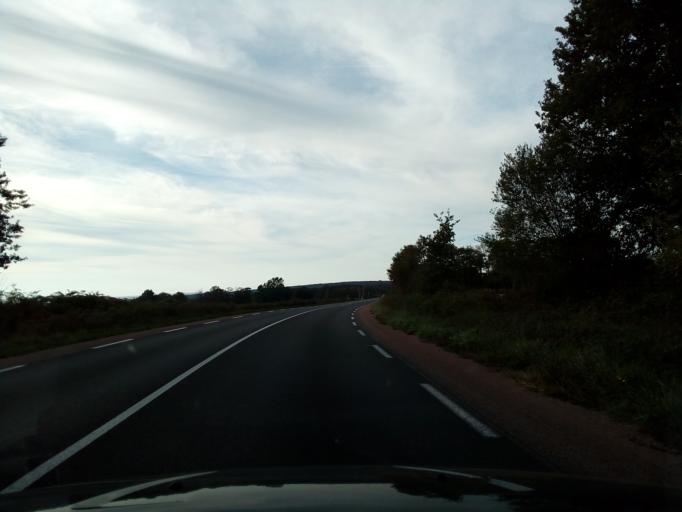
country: FR
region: Limousin
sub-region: Departement de la Haute-Vienne
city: Magnac-Laval
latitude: 46.1836
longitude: 1.2217
